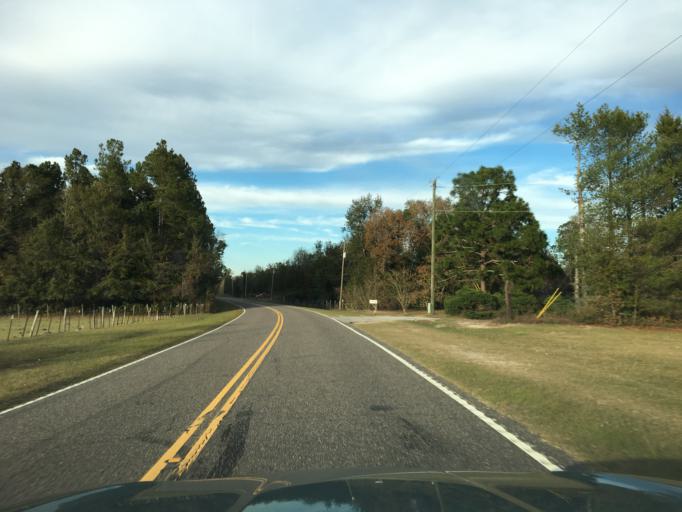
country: US
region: South Carolina
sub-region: Lexington County
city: Red Bank
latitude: 33.7039
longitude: -81.3567
